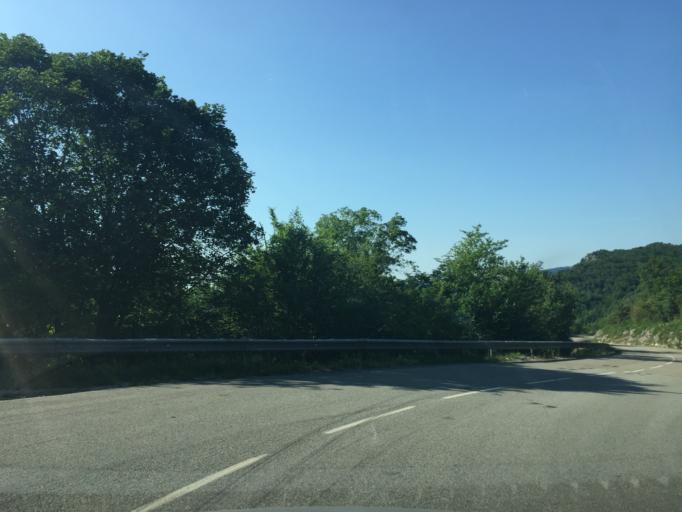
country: FR
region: Rhone-Alpes
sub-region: Departement de la Drome
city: Saint-Laurent-en-Royans
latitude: 45.0284
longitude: 5.3480
